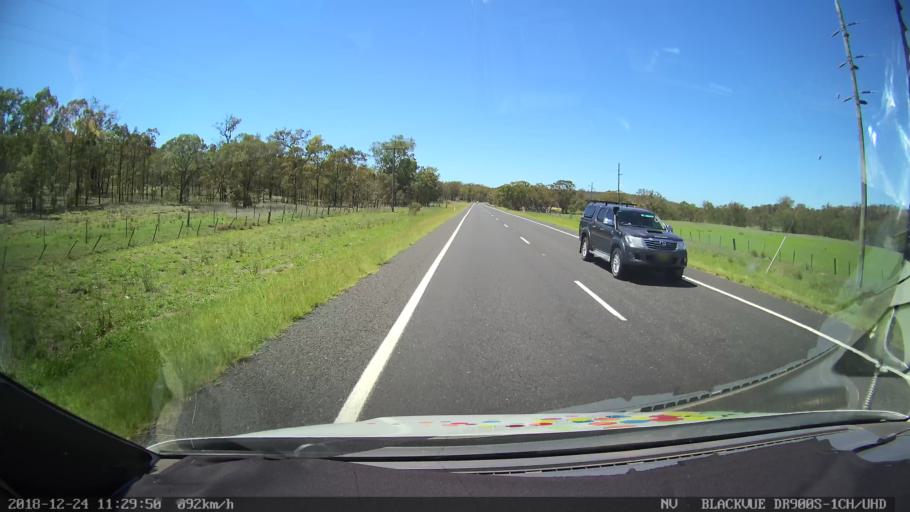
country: AU
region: New South Wales
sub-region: Upper Hunter Shire
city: Merriwa
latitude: -32.1972
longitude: 150.4654
